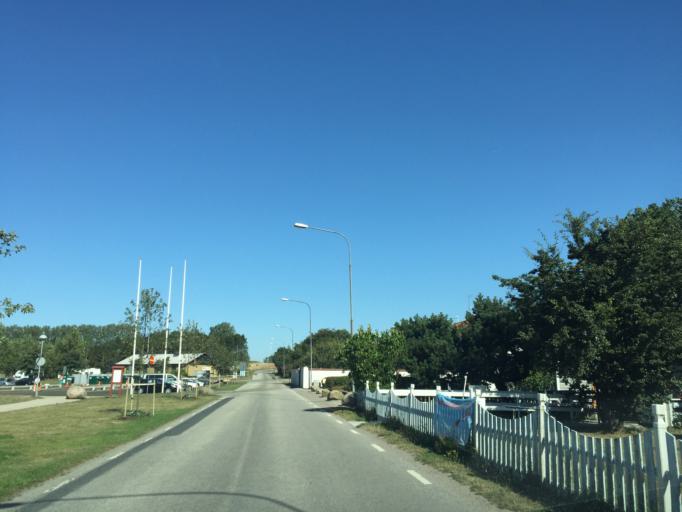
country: SE
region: Skane
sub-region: Ystads Kommun
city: Kopingebro
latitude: 55.3878
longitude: 14.0643
